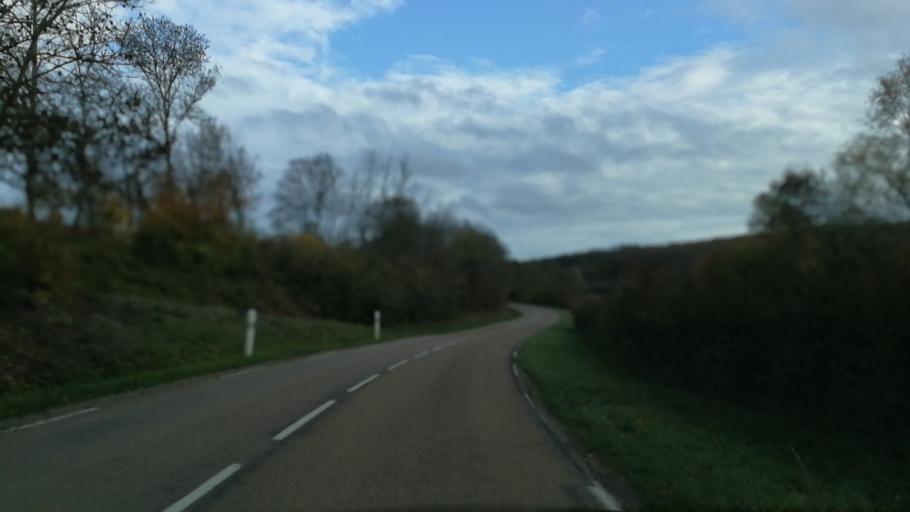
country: FR
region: Bourgogne
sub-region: Departement de la Cote-d'Or
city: Pouilly-en-Auxois
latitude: 47.2669
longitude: 4.4282
